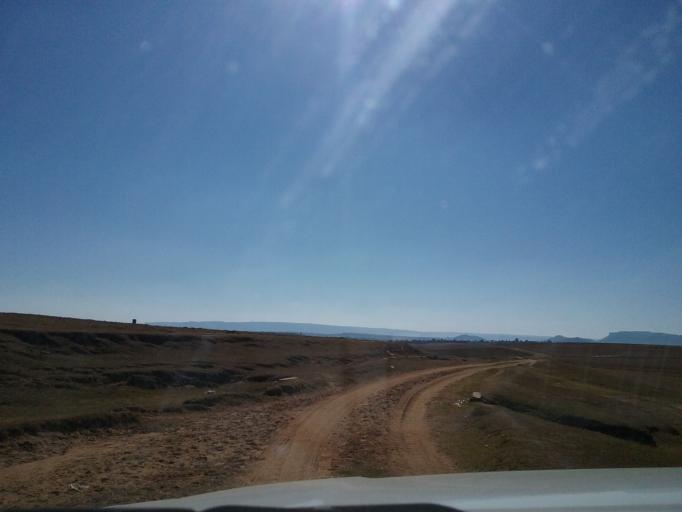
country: LS
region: Maseru
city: Nako
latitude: -29.4974
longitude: 27.5980
